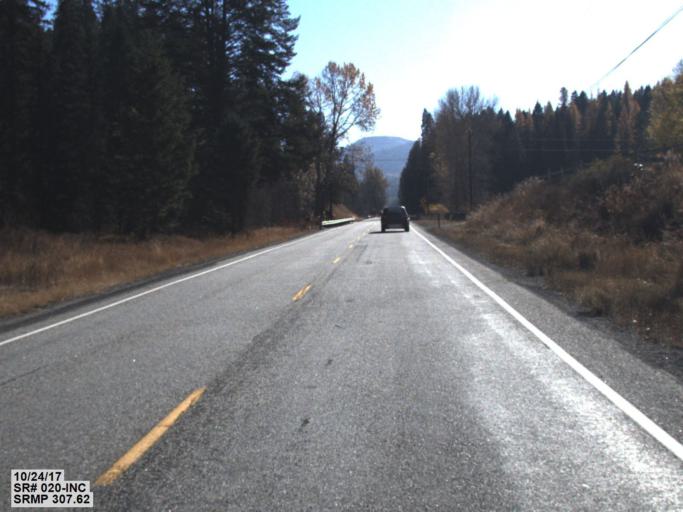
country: US
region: Washington
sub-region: Ferry County
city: Republic
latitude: 48.6193
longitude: -118.6693
